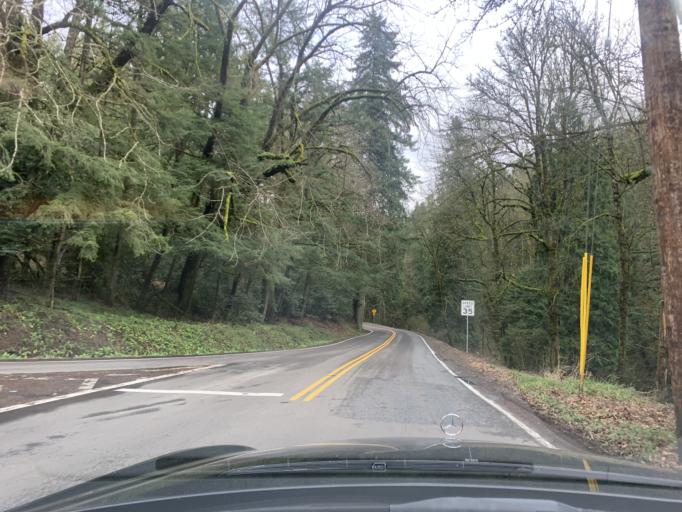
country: US
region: Oregon
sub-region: Multnomah County
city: Gresham
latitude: 45.4702
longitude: -122.4482
